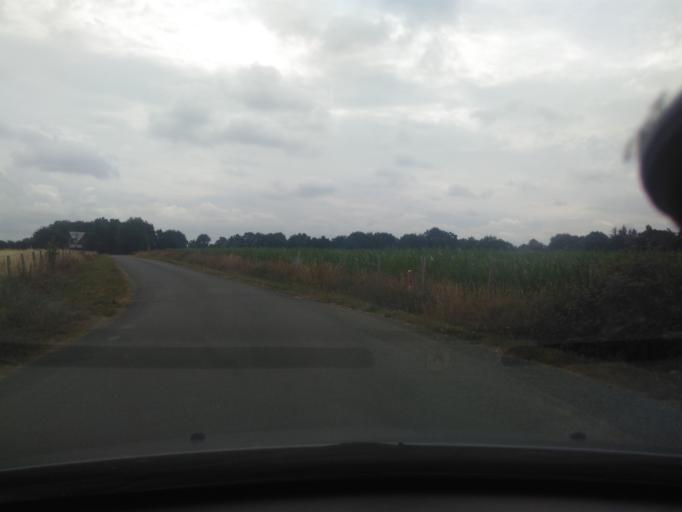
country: FR
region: Pays de la Loire
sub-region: Departement de la Vendee
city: La Ferriere
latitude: 46.7041
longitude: -1.3085
